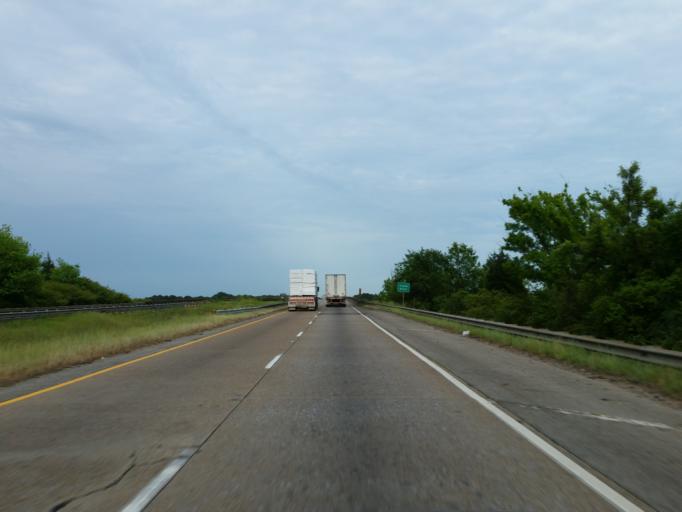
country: US
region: Alabama
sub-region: Saint Clair County
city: Riverside
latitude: 33.5941
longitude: -86.1878
